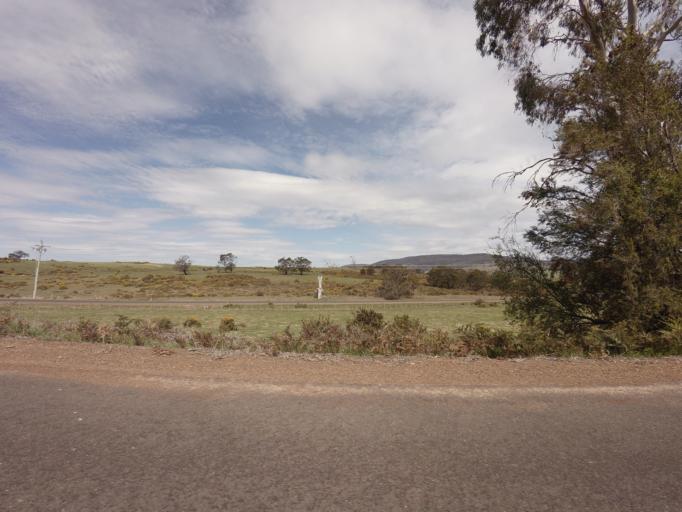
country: AU
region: Tasmania
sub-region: Northern Midlands
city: Evandale
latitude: -41.8950
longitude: 147.4087
